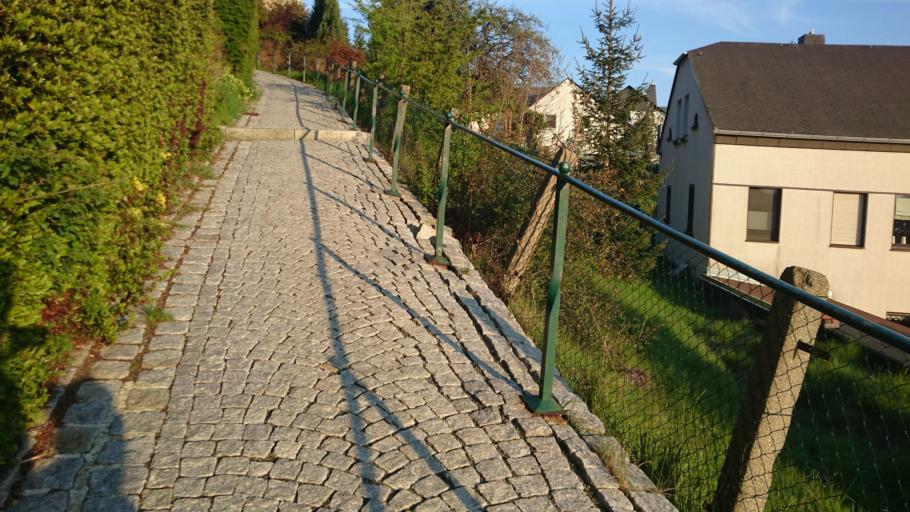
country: DE
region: Thuringia
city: Schleiz
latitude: 50.5750
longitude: 11.8130
